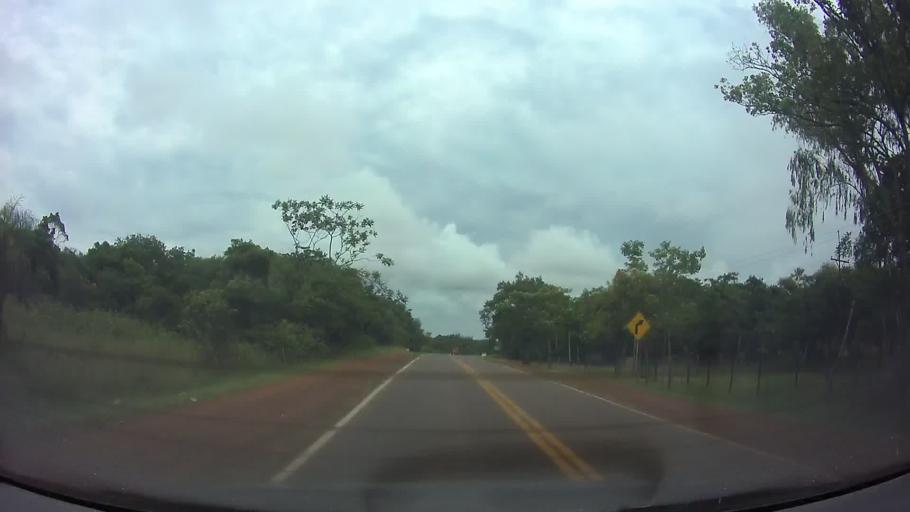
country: PY
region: Paraguari
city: Carapegua
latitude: -25.7966
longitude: -57.2008
